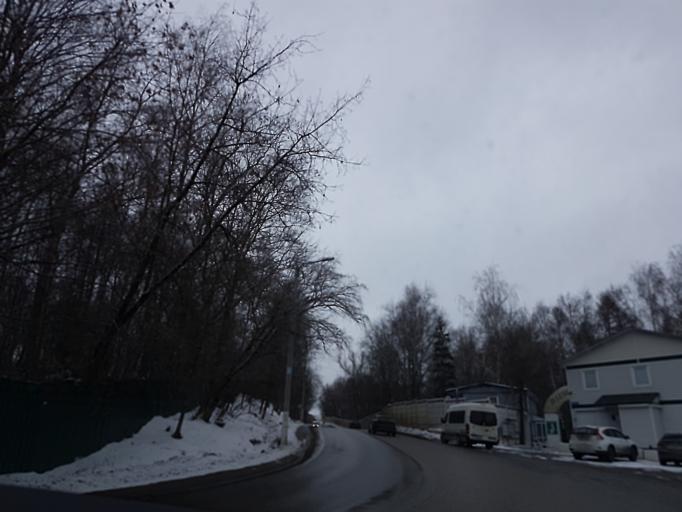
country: RU
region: Moskovskaya
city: Pavshino
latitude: 55.8200
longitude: 37.3589
